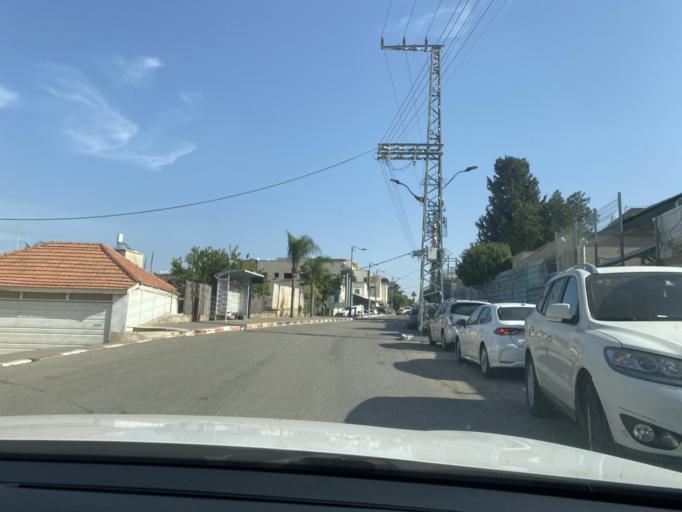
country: IL
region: Central District
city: Kafr Qasim
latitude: 32.1314
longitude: 34.9696
